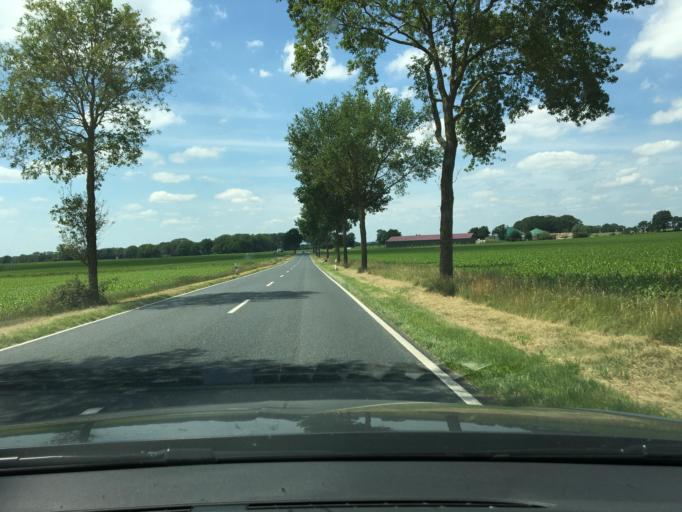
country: DE
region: Lower Saxony
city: Zeven
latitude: 53.2616
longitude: 9.2690
